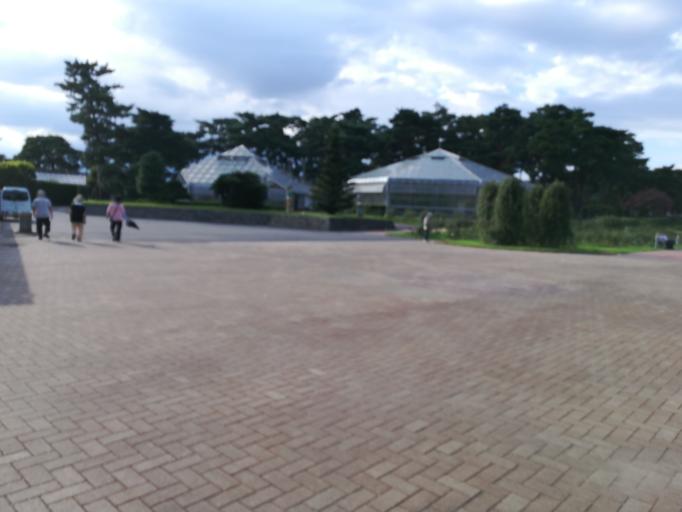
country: JP
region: Gunma
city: Maebashi-shi
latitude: 36.4184
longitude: 139.0494
